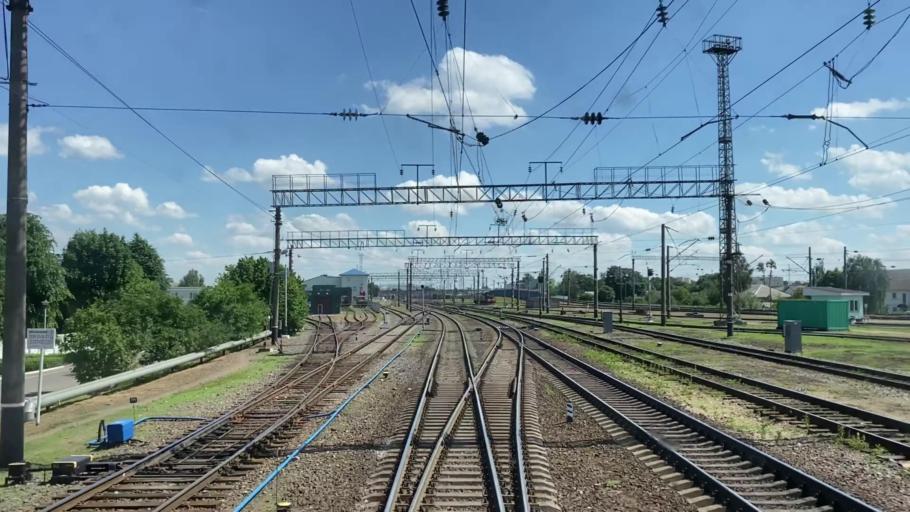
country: BY
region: Brest
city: Baranovichi
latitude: 53.1290
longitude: 25.9848
